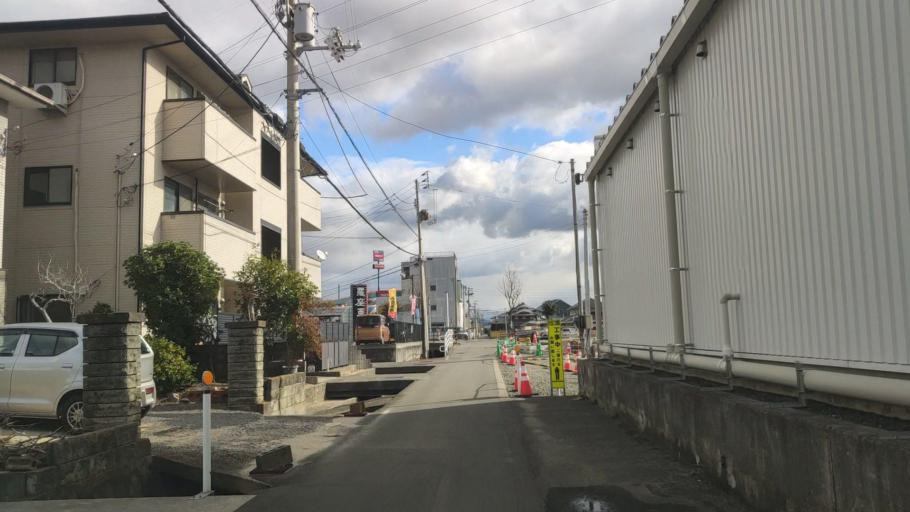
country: JP
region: Ehime
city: Masaki-cho
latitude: 33.8116
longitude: 132.7342
